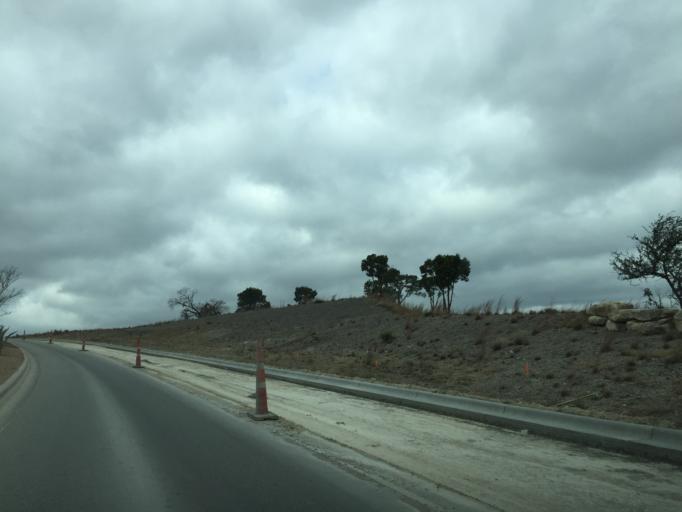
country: US
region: Texas
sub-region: Travis County
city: The Hills
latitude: 30.3458
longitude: -98.0238
